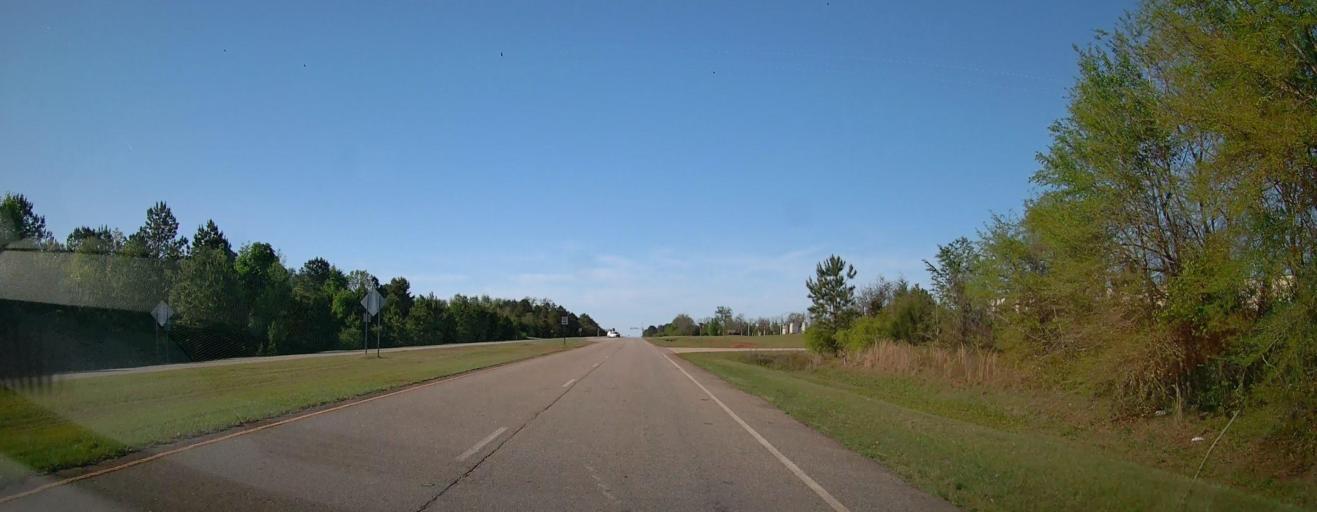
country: US
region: Georgia
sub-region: Houston County
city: Perry
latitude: 32.4596
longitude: -83.7782
